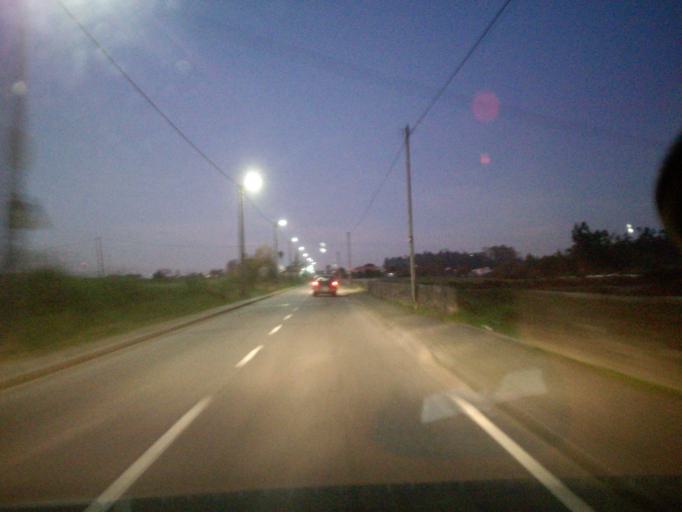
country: PT
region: Porto
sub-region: Maia
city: Nogueira
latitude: 41.2481
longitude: -8.5849
